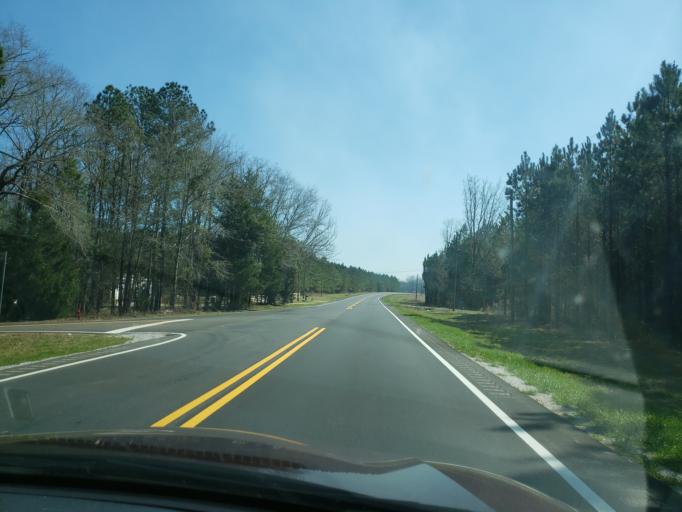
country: US
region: Alabama
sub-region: Macon County
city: Tuskegee
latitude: 32.5758
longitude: -85.6924
